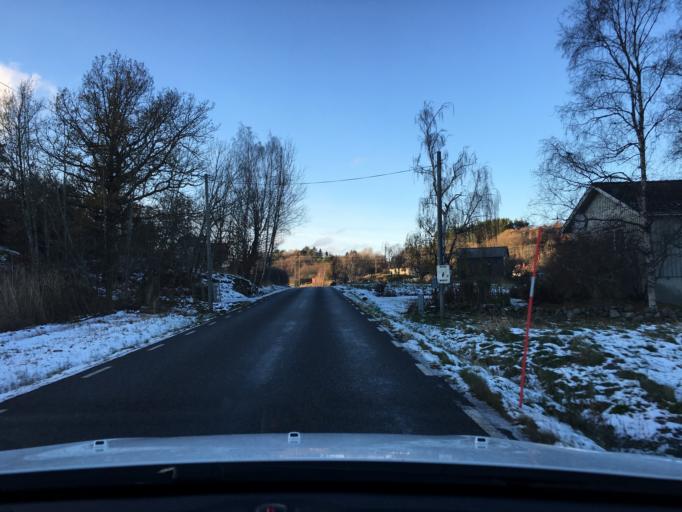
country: SE
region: Vaestra Goetaland
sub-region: Tjorns Kommun
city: Myggenas
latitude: 58.0543
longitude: 11.6987
